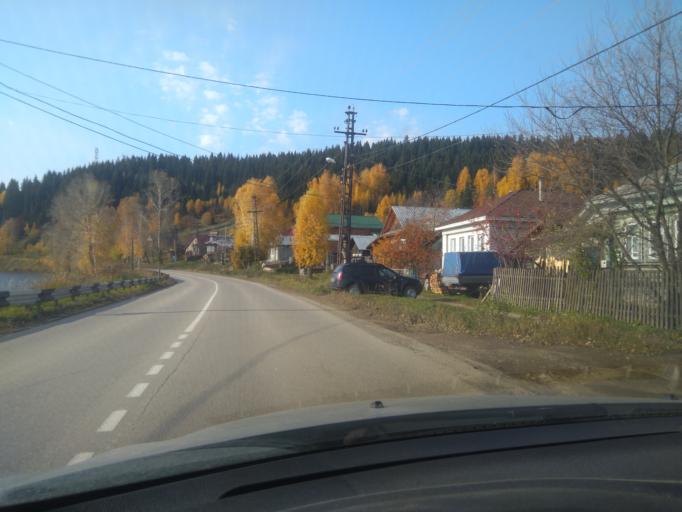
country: RU
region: Sverdlovsk
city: Nizhniye Sergi
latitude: 56.6752
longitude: 59.3220
